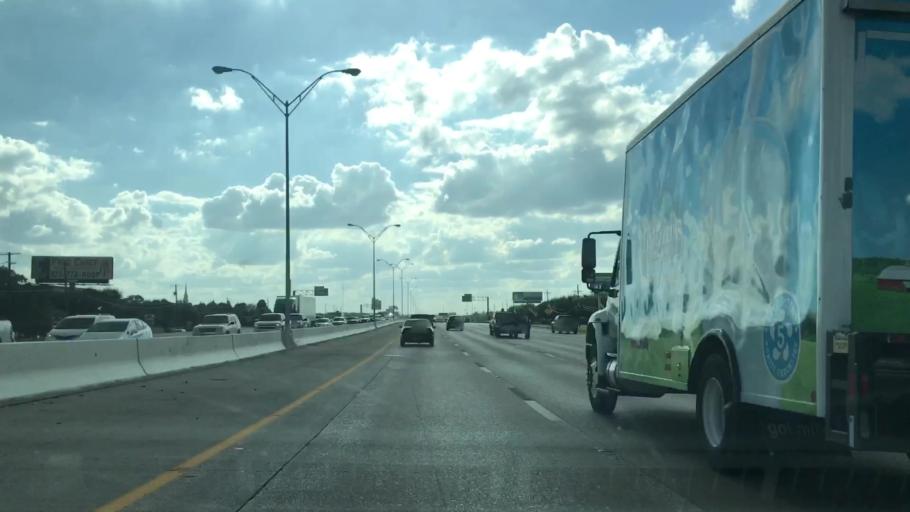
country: US
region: Texas
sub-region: Dallas County
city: Sunnyvale
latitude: 32.8491
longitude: -96.5734
